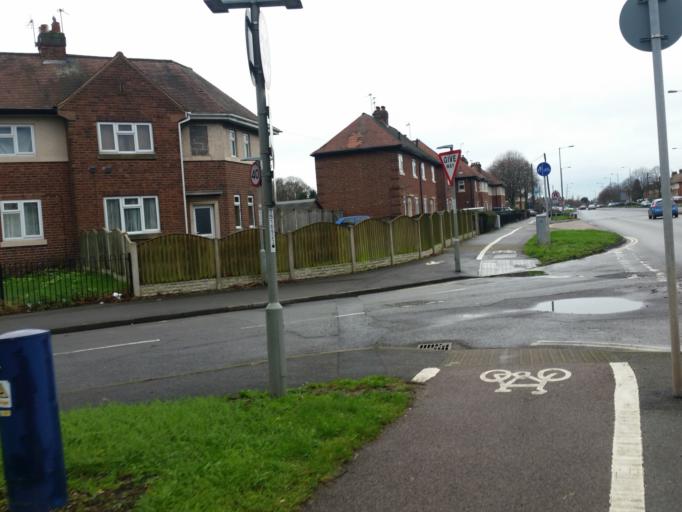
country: GB
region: England
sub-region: Derbyshire
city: Borrowash
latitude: 52.8954
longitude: -1.4287
